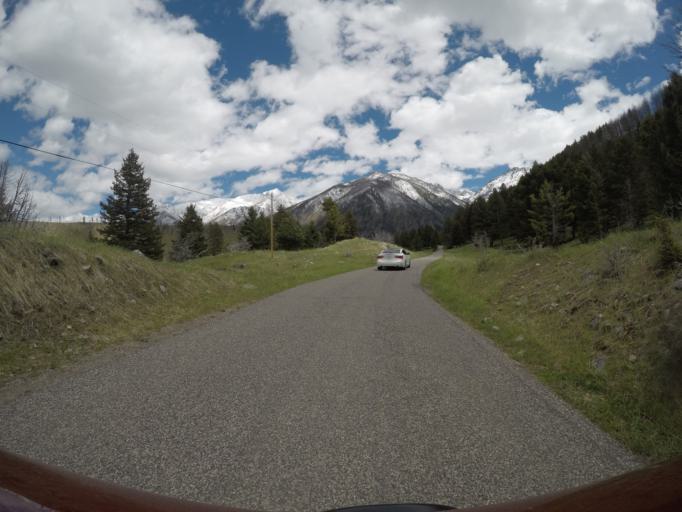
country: US
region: Montana
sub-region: Park County
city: Livingston
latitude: 45.4999
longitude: -110.5430
